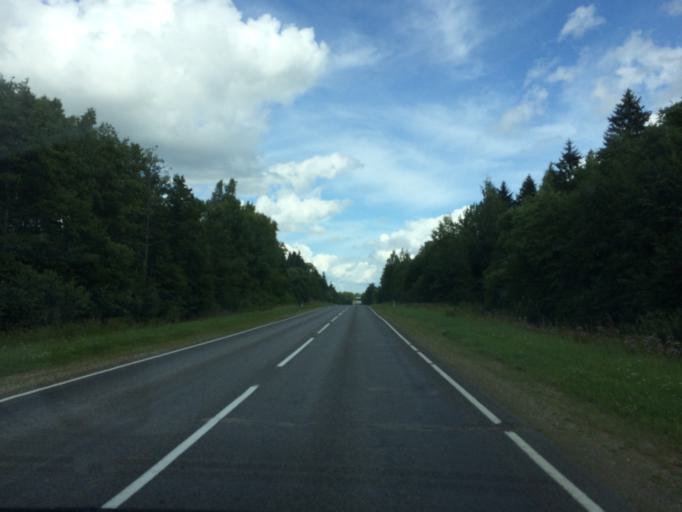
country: LV
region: Rezekne
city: Rezekne
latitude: 56.6168
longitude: 27.4502
